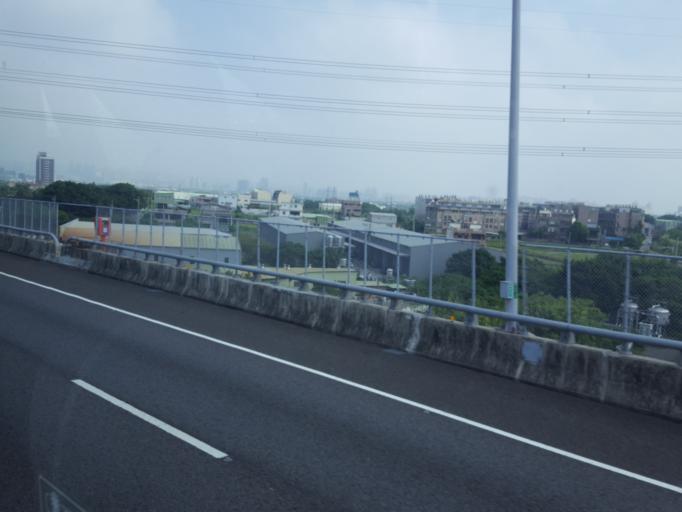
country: TW
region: Taiwan
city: Taoyuan City
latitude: 24.9995
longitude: 121.2496
